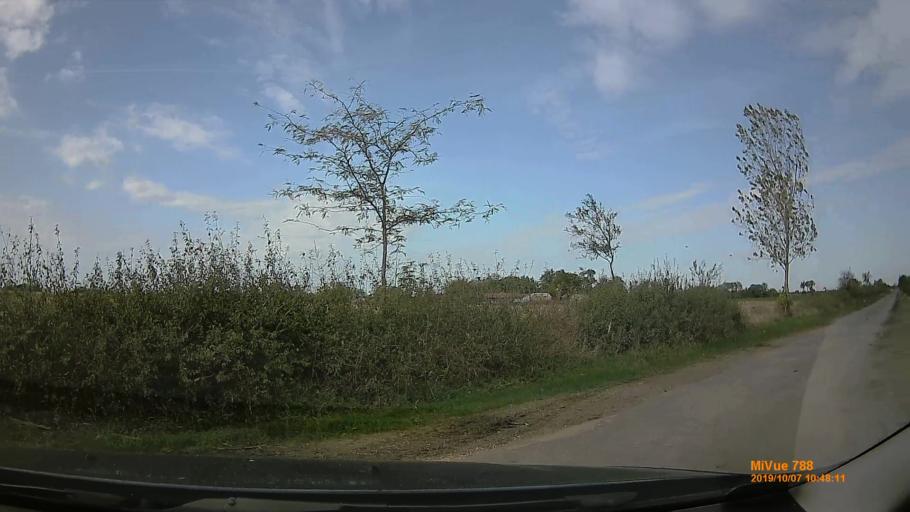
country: HU
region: Bekes
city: Kondoros
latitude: 46.7311
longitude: 20.8119
